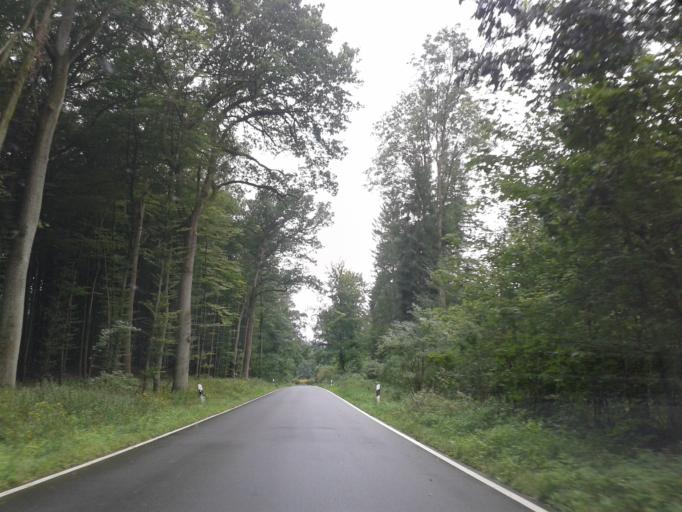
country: DE
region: North Rhine-Westphalia
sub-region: Regierungsbezirk Detmold
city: Barntrup
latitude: 51.9574
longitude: 9.1343
